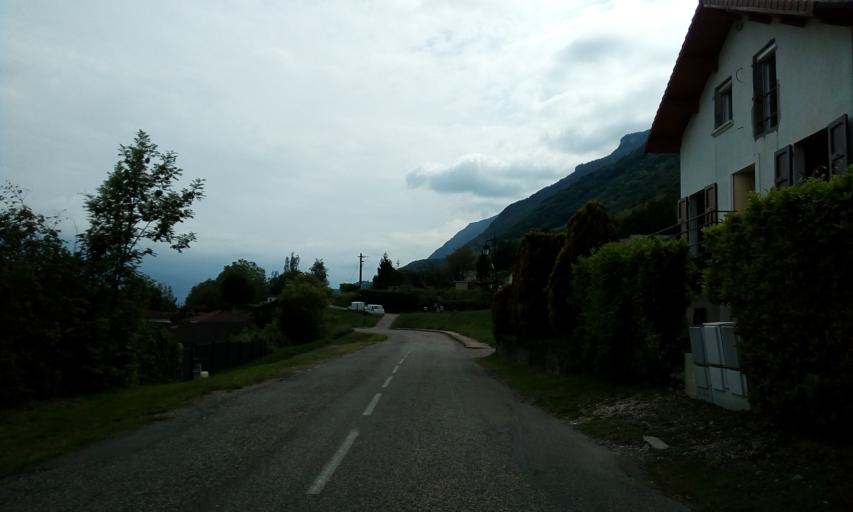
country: FR
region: Rhone-Alpes
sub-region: Departement de l'Isere
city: Saint-Vincent-de-Mercuze
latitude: 45.3850
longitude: 5.9525
